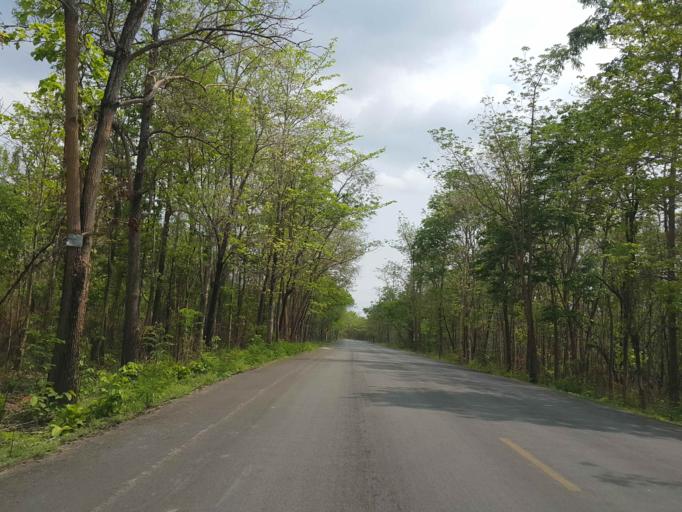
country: TH
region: Lampang
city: Thoen
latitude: 17.4474
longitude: 99.3718
